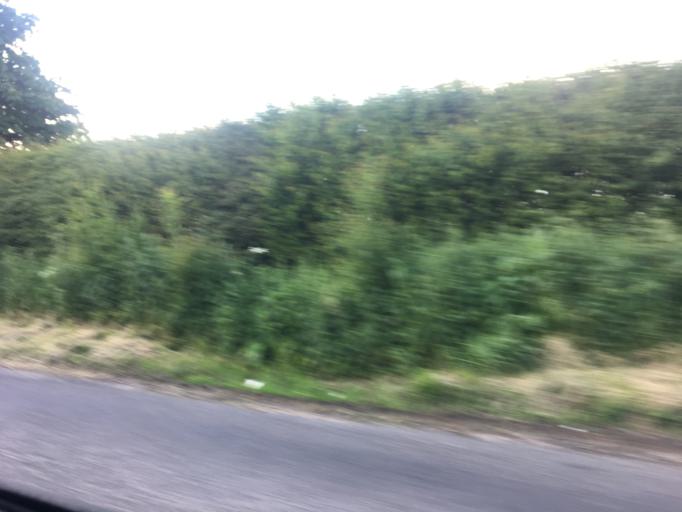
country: GB
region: England
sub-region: Leicestershire
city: Oadby
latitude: 52.6133
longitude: -1.0480
